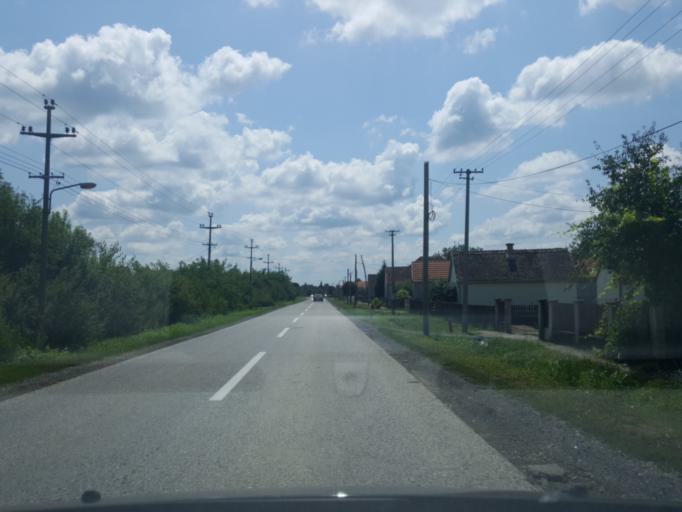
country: RS
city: Metkovic
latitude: 44.8621
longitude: 19.5444
